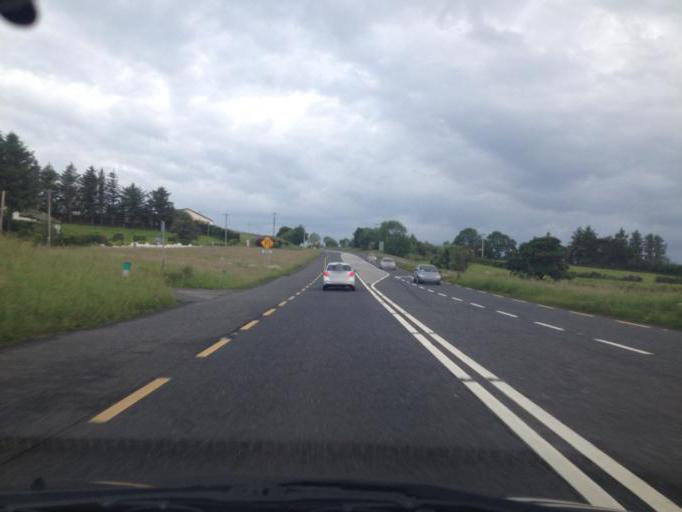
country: IE
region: Connaught
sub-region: Sligo
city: Strandhill
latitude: 54.3727
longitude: -8.5300
